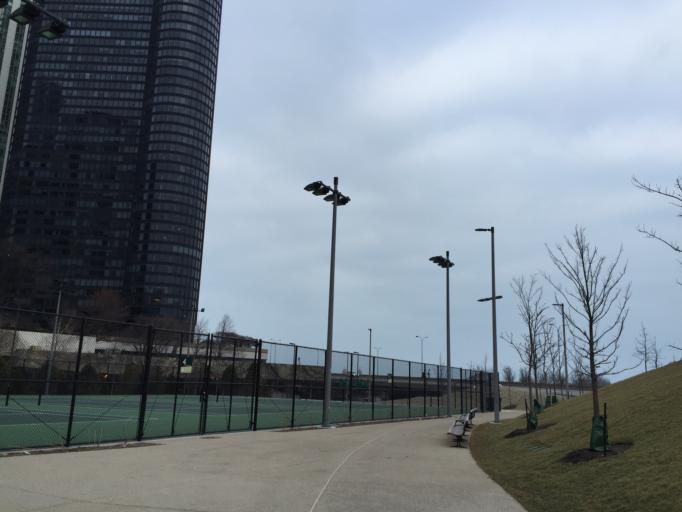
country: US
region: Illinois
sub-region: Cook County
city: Chicago
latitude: 41.8836
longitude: -87.6159
